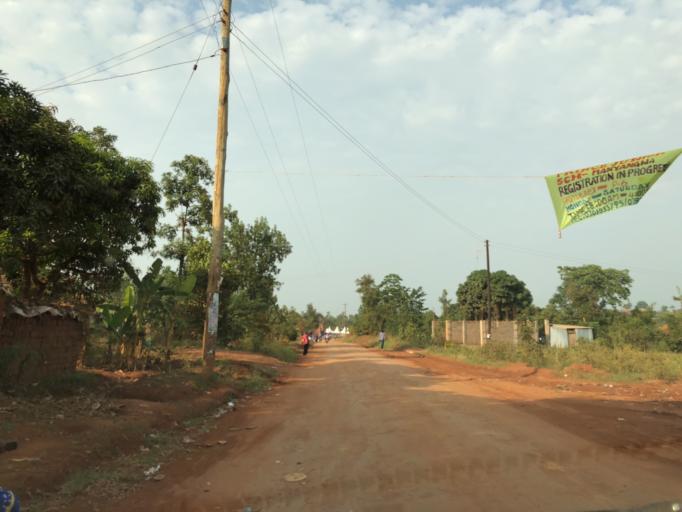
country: UG
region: Central Region
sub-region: Wakiso District
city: Bweyogerere
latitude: 0.4688
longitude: 32.6304
